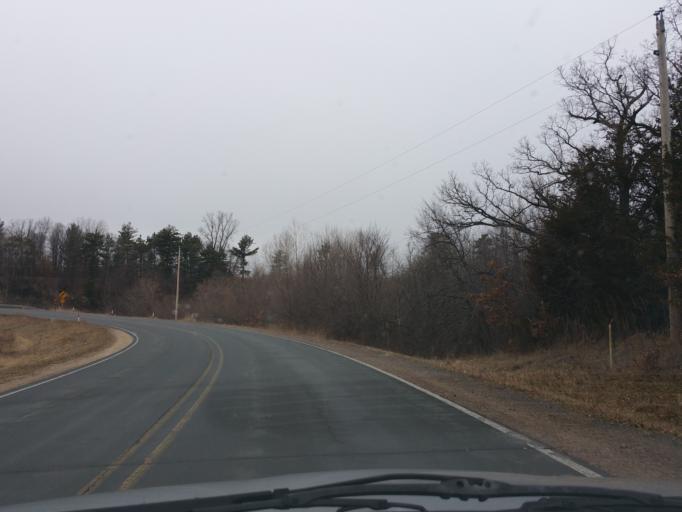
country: US
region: Wisconsin
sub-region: Saint Croix County
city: Somerset
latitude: 45.0368
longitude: -92.6367
